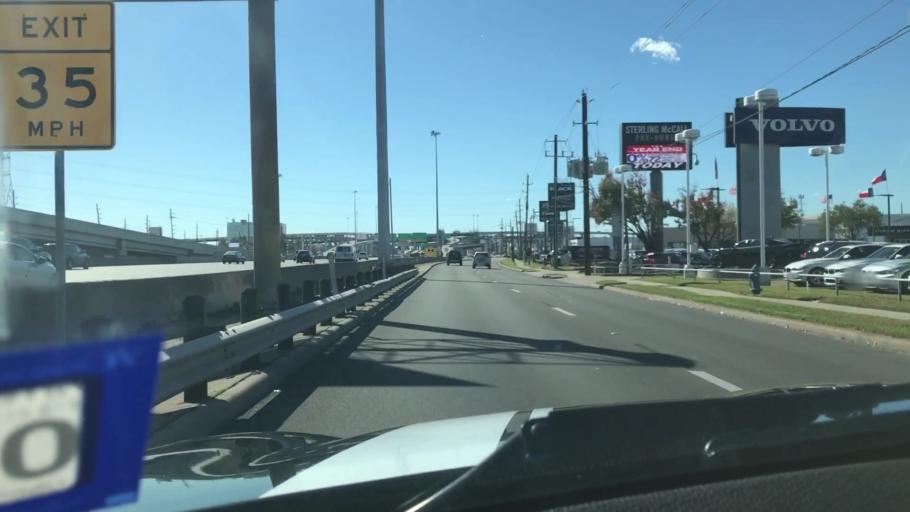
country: US
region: Texas
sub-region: Fort Bend County
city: Meadows Place
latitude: 29.6686
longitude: -95.5503
